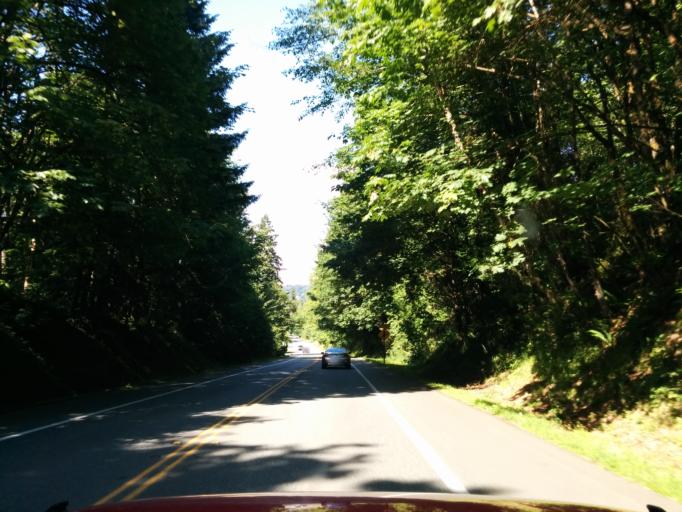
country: US
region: Washington
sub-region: King County
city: West Lake Sammamish
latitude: 47.5943
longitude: -122.0830
